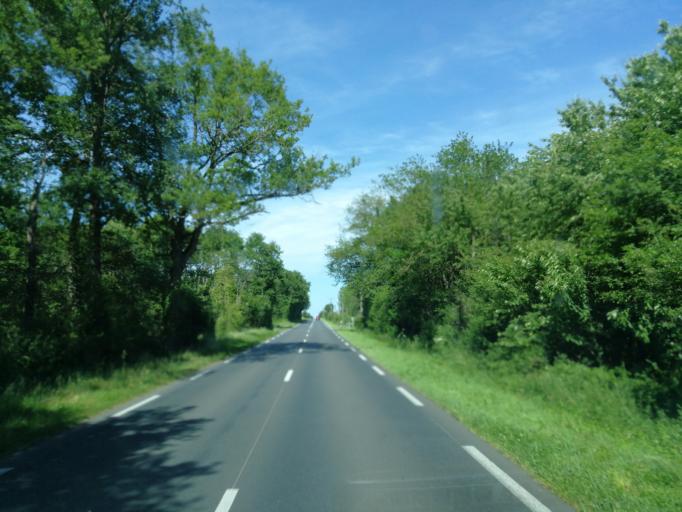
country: FR
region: Poitou-Charentes
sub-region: Departement des Deux-Sevres
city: Saint-Jean-de-Thouars
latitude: 46.9385
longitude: -0.2416
